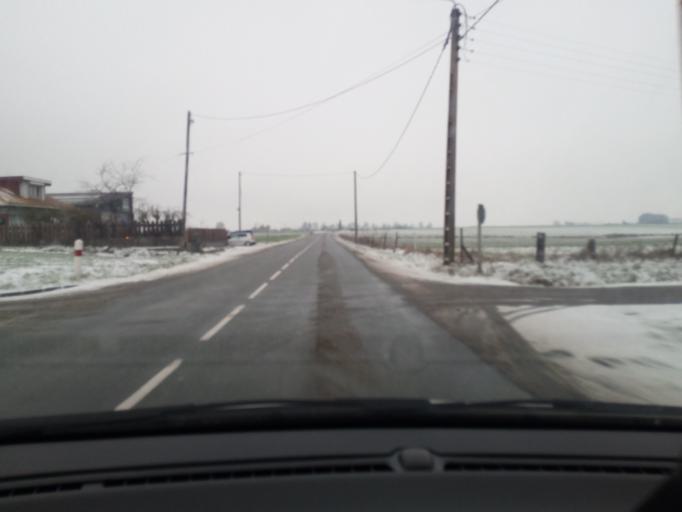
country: FR
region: Nord-Pas-de-Calais
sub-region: Departement du Nord
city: La Longueville
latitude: 50.3335
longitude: 3.8711
